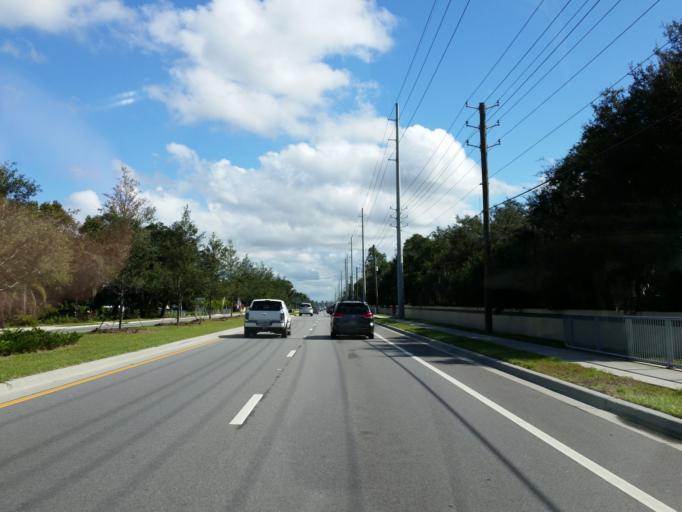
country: US
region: Florida
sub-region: Hillsborough County
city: Riverview
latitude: 27.8534
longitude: -82.2954
